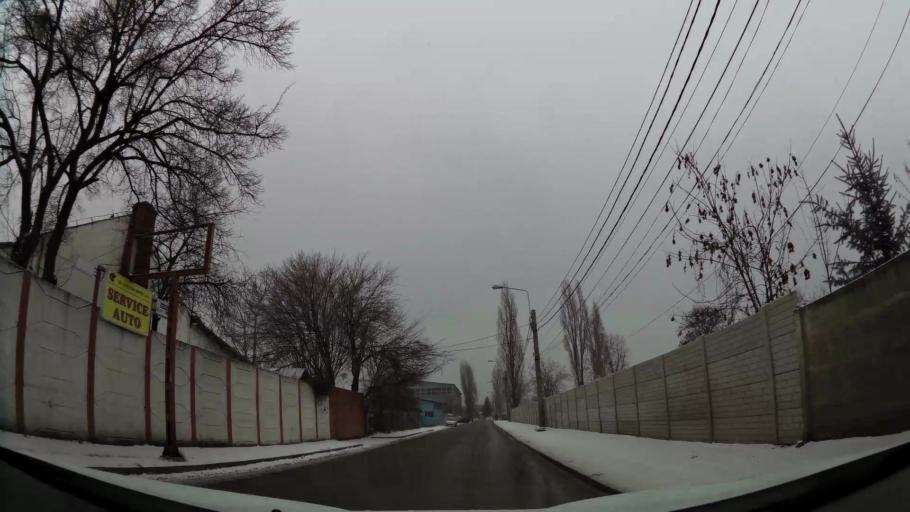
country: RO
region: Prahova
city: Ploiesti
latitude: 44.9250
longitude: 26.0066
